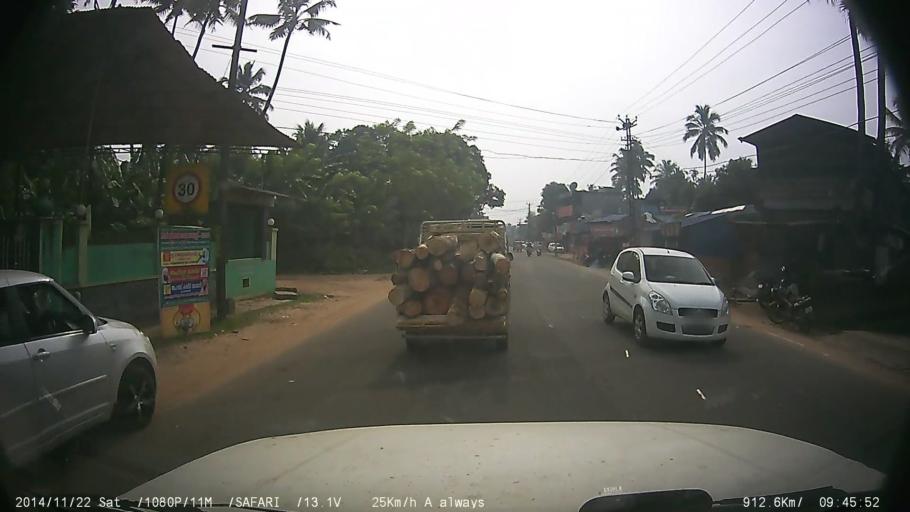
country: IN
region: Kerala
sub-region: Ernakulam
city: Perumpavur
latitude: 10.1373
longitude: 76.4658
